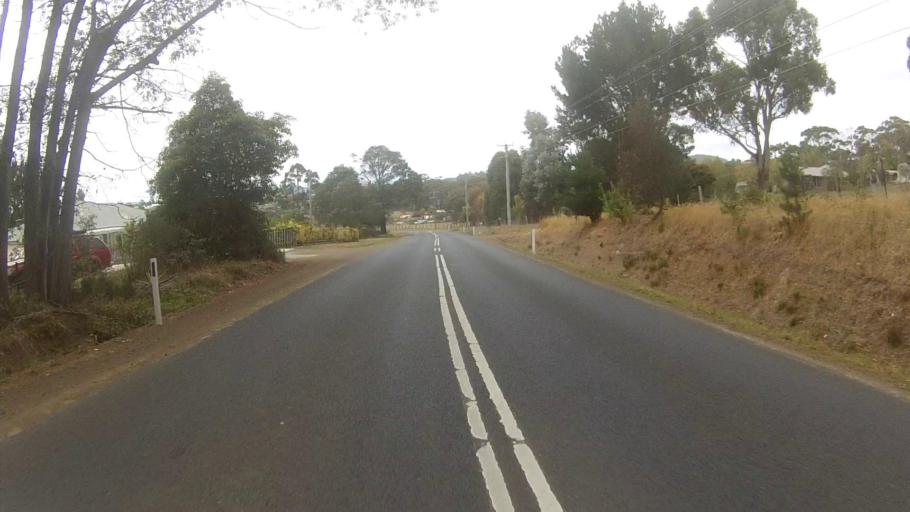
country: AU
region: Tasmania
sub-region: Kingborough
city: Margate
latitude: -43.0191
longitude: 147.2535
